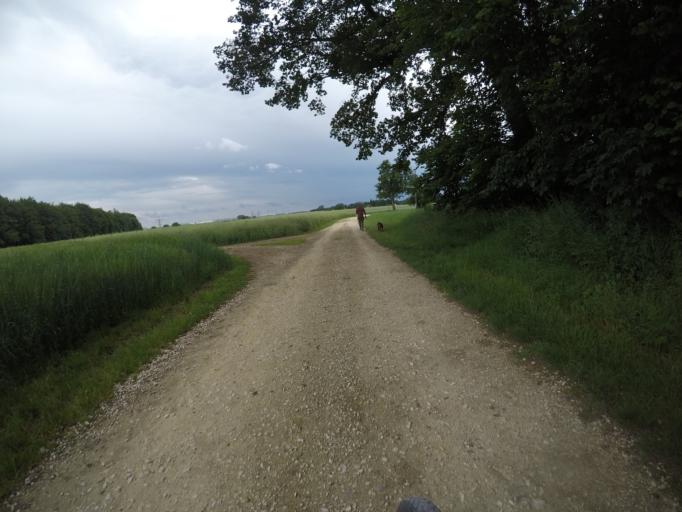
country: DE
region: Baden-Wuerttemberg
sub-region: Tuebingen Region
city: Dornstadt
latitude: 48.4779
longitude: 9.9575
